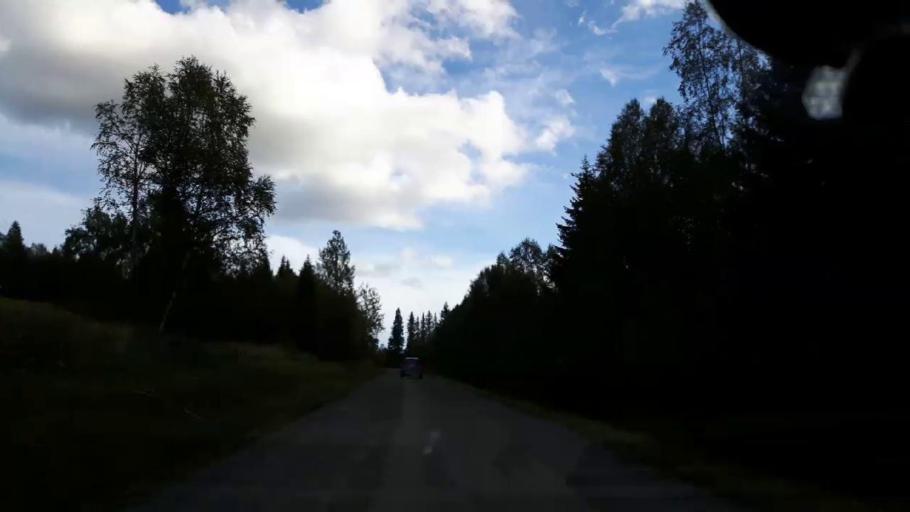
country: SE
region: Jaemtland
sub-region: Ragunda Kommun
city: Hammarstrand
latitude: 63.4159
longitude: 16.0784
